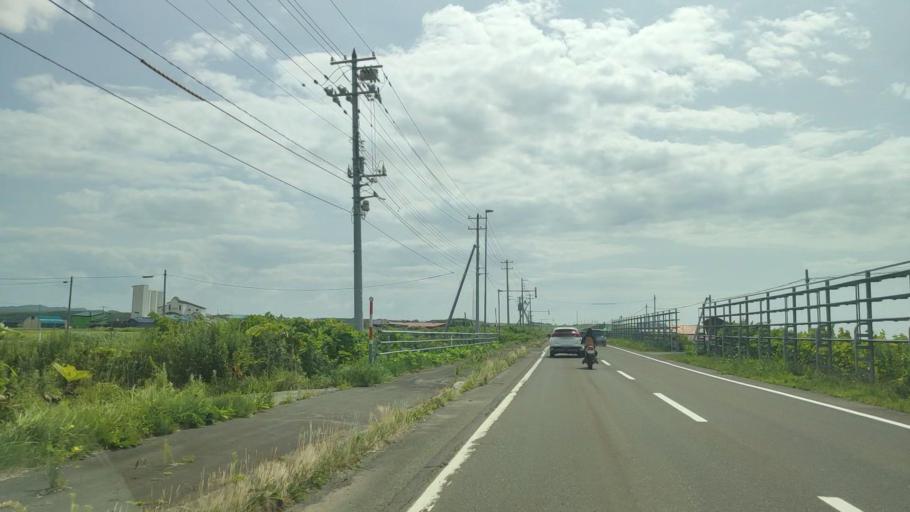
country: JP
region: Hokkaido
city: Rumoi
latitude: 44.4529
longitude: 141.7586
